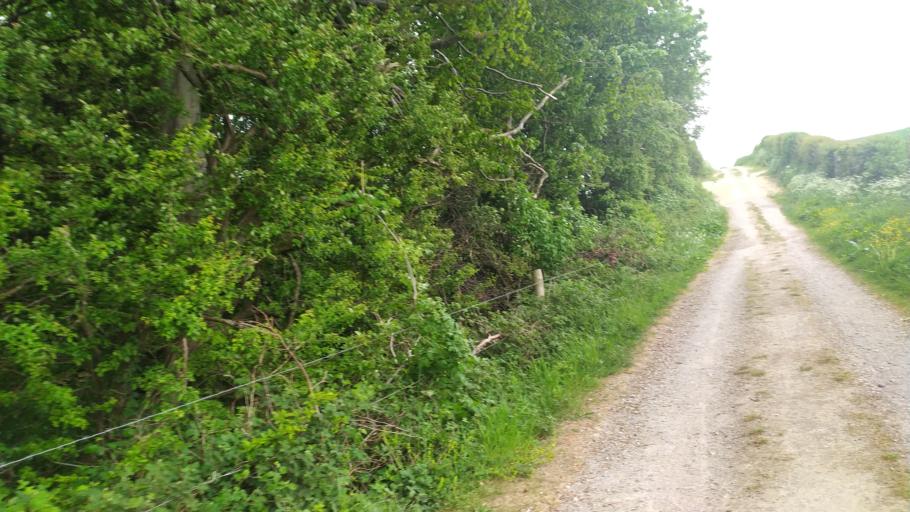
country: GB
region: England
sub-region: City and Borough of Leeds
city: Thorner
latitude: 53.8571
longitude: -1.3903
